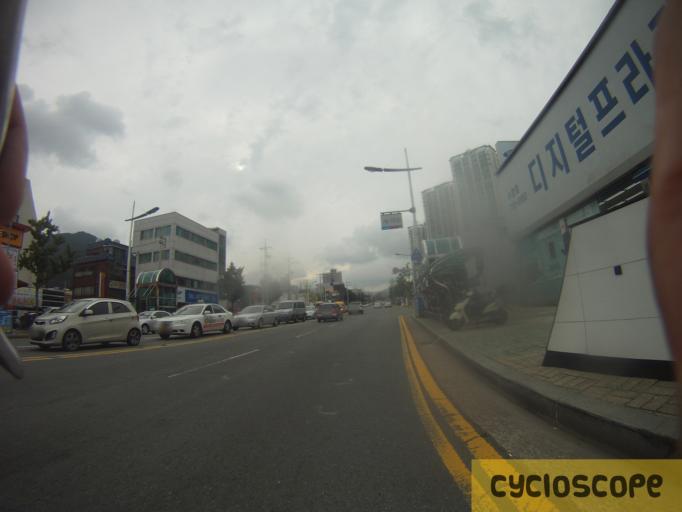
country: KR
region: Busan
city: Busan
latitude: 35.1718
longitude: 129.1082
